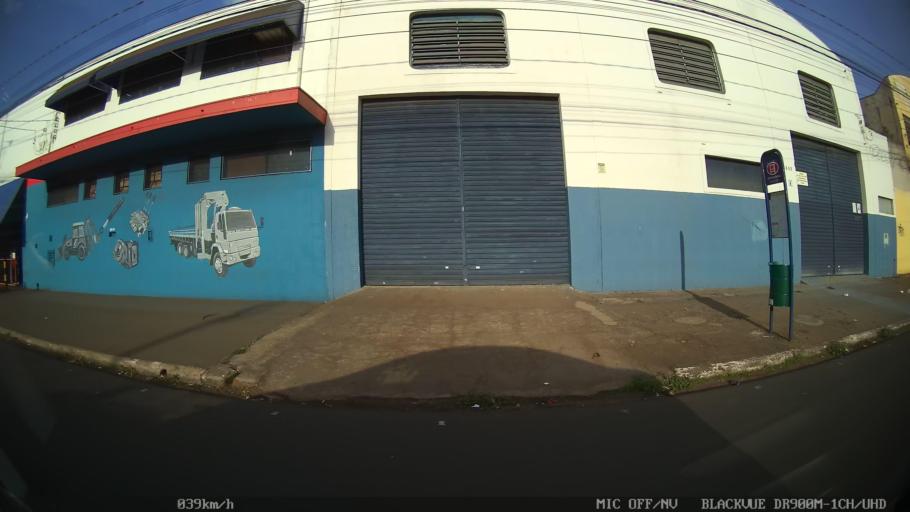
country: BR
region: Sao Paulo
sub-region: Ribeirao Preto
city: Ribeirao Preto
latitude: -21.1365
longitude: -47.7969
